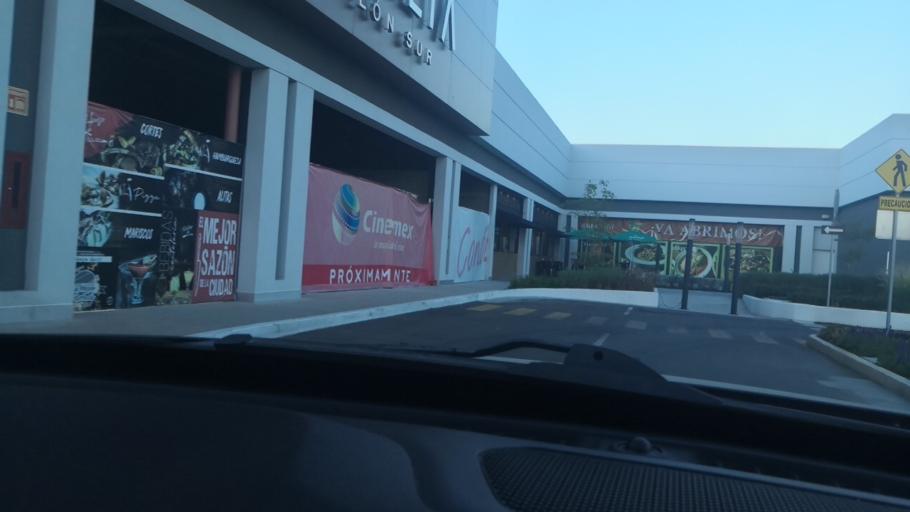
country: MX
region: Guanajuato
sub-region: Leon
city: Fraccionamiento Paraiso Real
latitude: 21.0801
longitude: -101.6054
